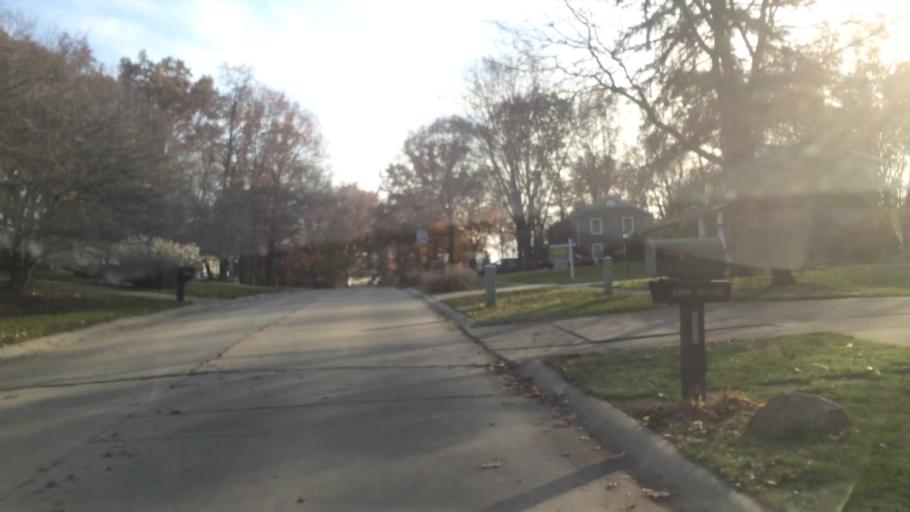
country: US
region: Ohio
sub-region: Summit County
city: Silver Lake
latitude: 41.1824
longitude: -81.4548
